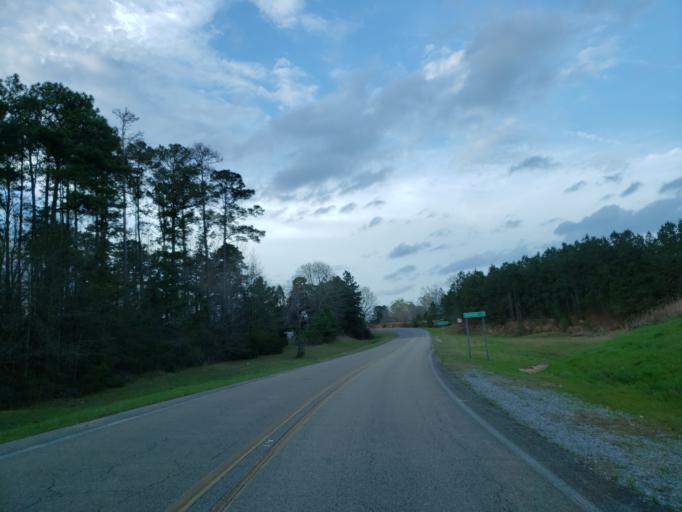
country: US
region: Mississippi
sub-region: Clarke County
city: Stonewall
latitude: 32.2142
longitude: -88.6991
